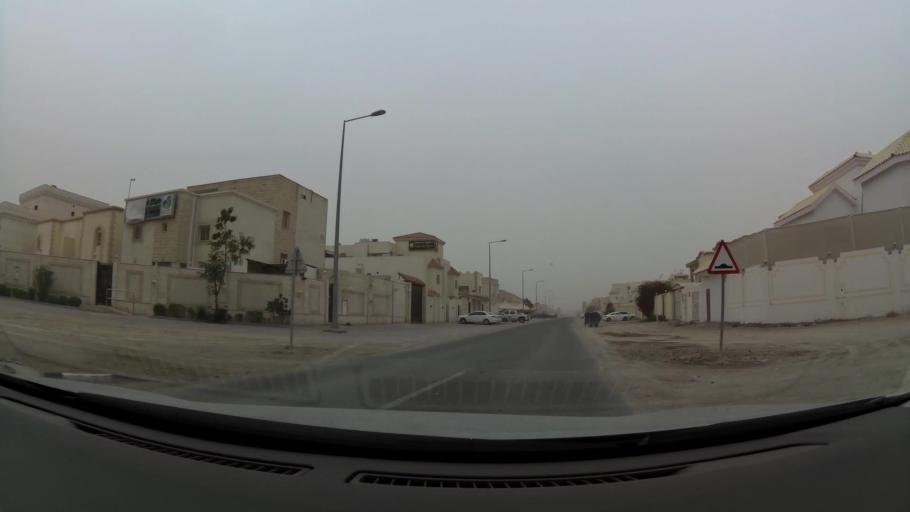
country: QA
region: Baladiyat ad Dawhah
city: Doha
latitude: 25.2425
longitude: 51.4887
